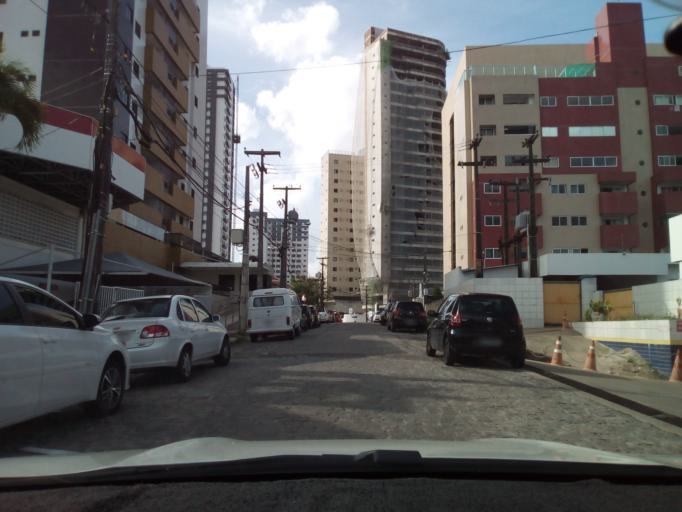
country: BR
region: Paraiba
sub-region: Joao Pessoa
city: Joao Pessoa
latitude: -7.1195
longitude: -34.8409
